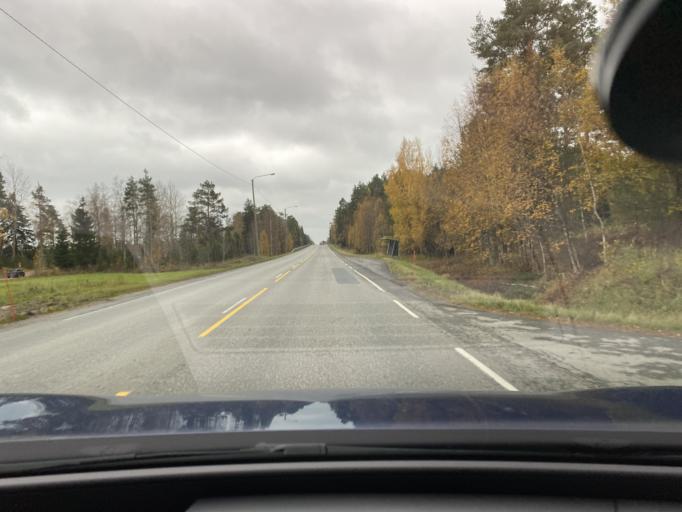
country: FI
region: Varsinais-Suomi
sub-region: Vakka-Suomi
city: Laitila
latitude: 60.9699
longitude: 21.5938
